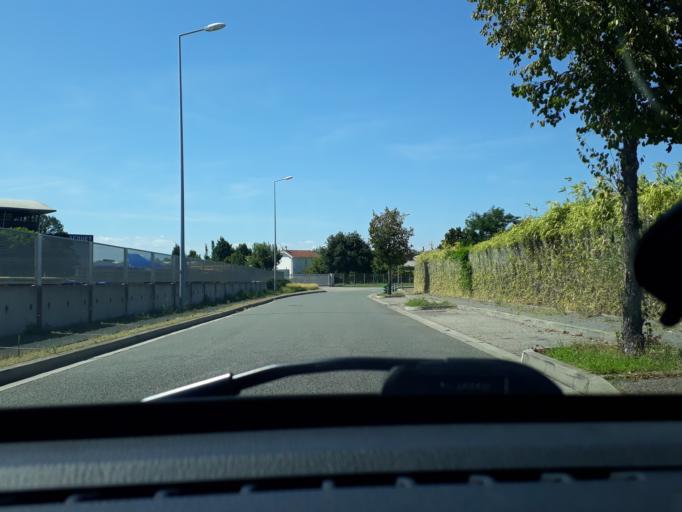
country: FR
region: Rhone-Alpes
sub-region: Departement du Rhone
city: Saint-Priest
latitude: 45.6959
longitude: 4.9202
